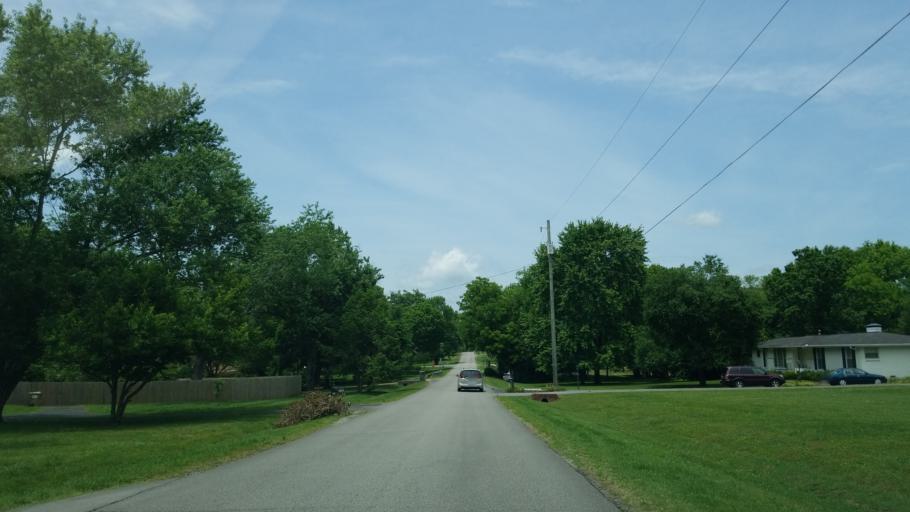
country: US
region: Tennessee
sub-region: Williamson County
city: Brentwood
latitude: 36.0296
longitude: -86.8010
